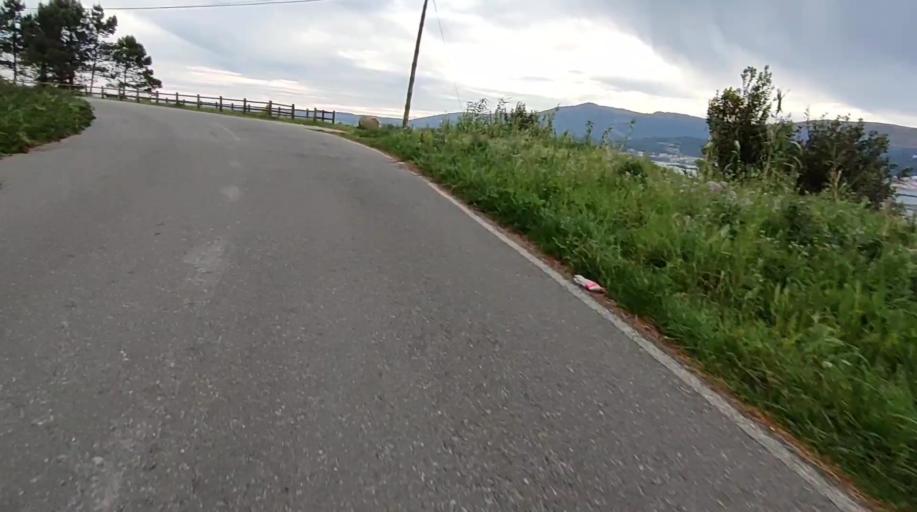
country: ES
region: Galicia
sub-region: Provincia da Coruna
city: Boiro
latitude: 42.6218
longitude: -8.8857
